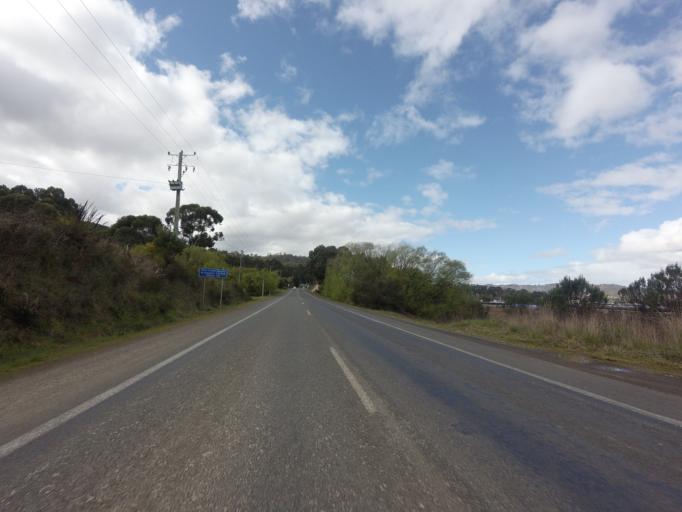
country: AU
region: Tasmania
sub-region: Huon Valley
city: Geeveston
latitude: -43.1577
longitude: 146.9549
